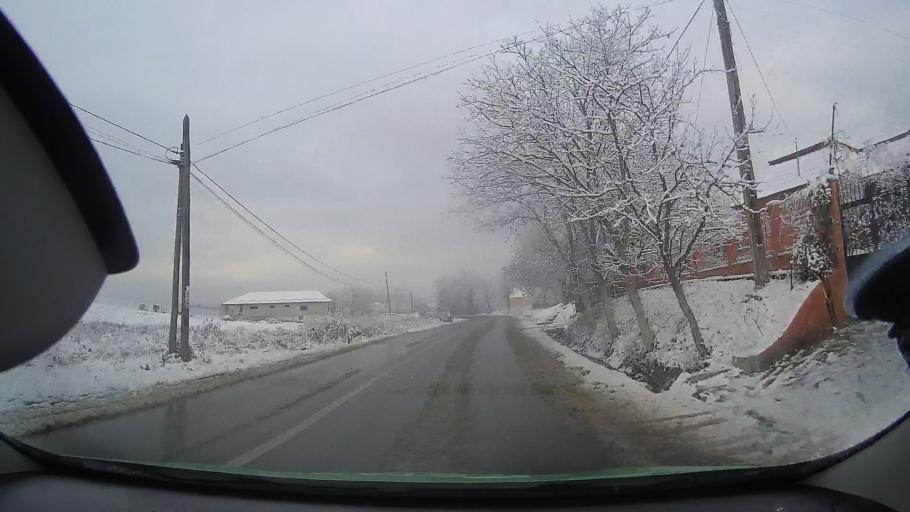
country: RO
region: Mures
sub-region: Comuna Bogata
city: Bogata
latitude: 46.4504
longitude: 24.0853
